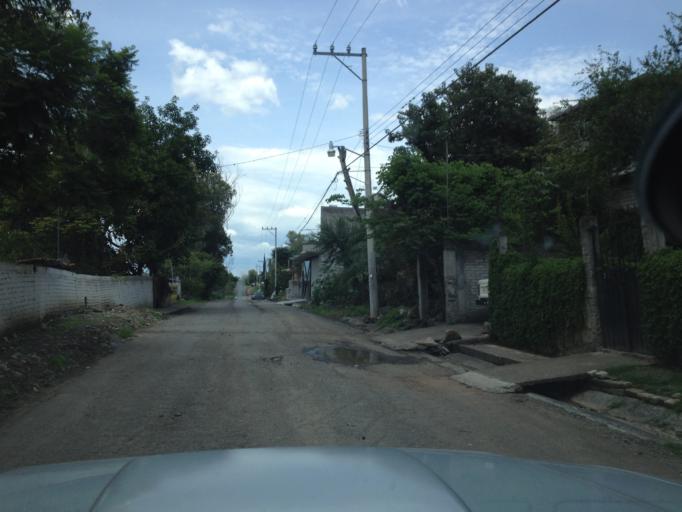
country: MX
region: Michoacan
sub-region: Tarimbaro
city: El Colegio
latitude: 19.7732
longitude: -101.1738
